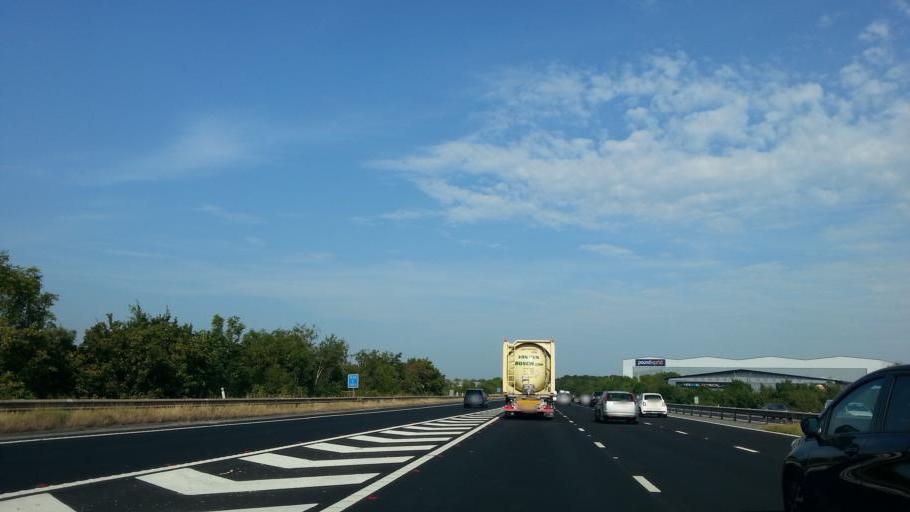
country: GB
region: England
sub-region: City and Borough of Wakefield
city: Normanton
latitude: 53.7084
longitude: -1.3896
